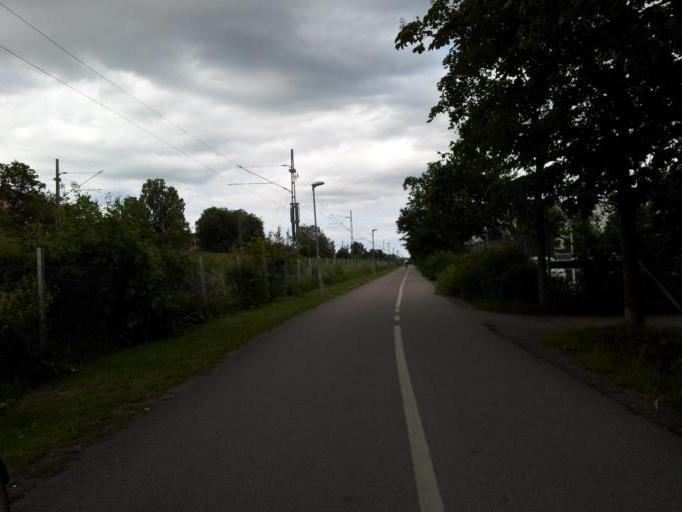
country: SE
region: Uppsala
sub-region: Uppsala Kommun
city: Uppsala
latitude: 59.8660
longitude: 17.6361
